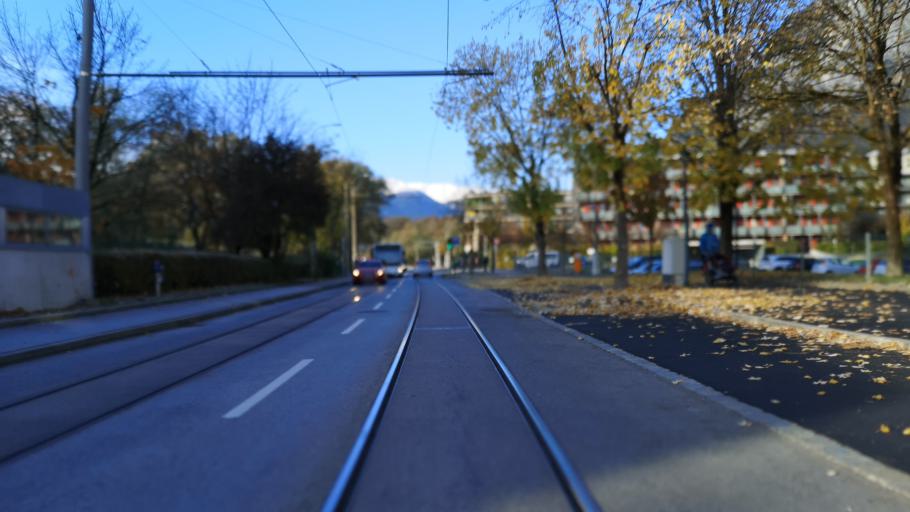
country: AT
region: Tyrol
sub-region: Politischer Bezirk Innsbruck Land
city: Vols
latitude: 47.2653
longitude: 11.3422
